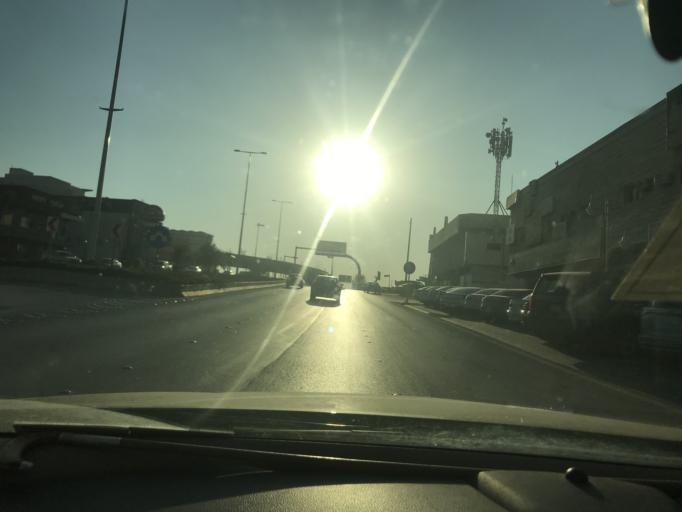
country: SA
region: Ar Riyad
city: Riyadh
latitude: 24.7412
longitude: 46.7498
